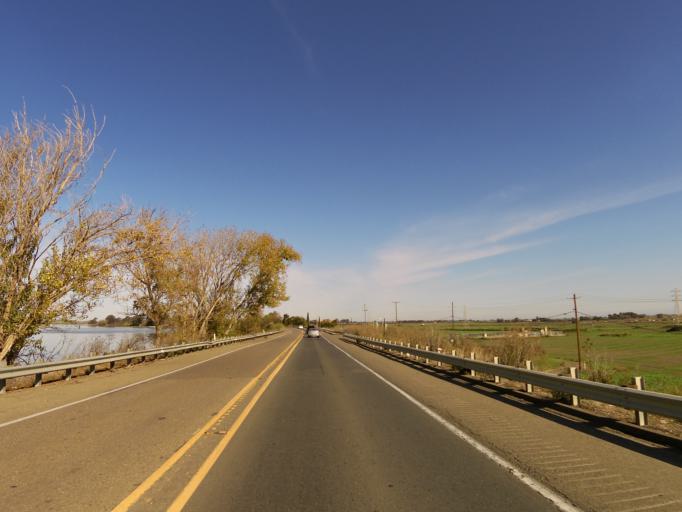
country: US
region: California
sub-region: Solano County
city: Rio Vista
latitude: 38.0850
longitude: -121.7087
